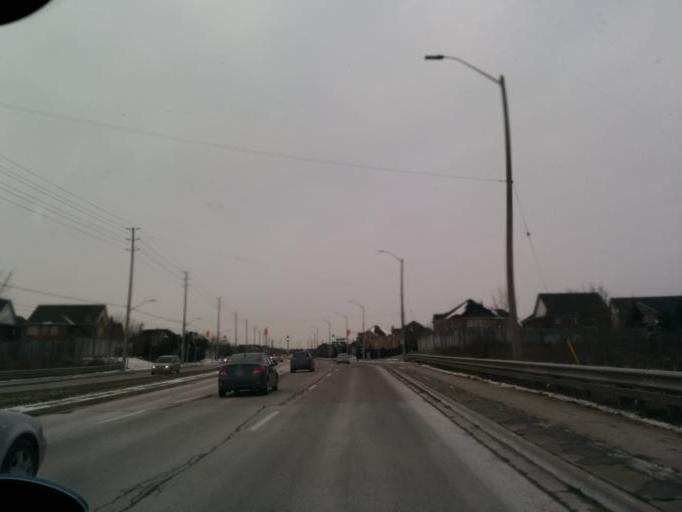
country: CA
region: Ontario
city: Mississauga
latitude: 43.6270
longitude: -79.7157
